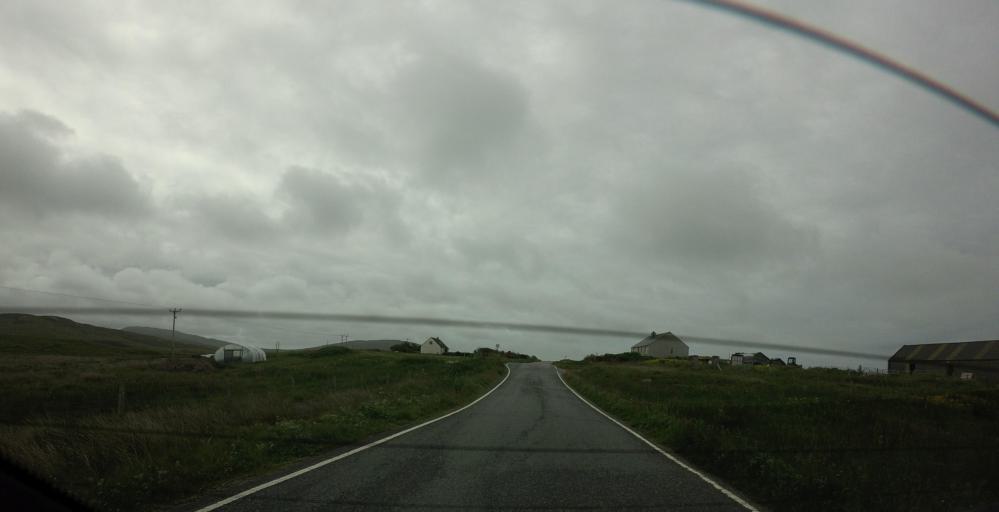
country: GB
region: Scotland
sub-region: Eilean Siar
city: Isle of South Uist
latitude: 57.2110
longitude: -7.3940
